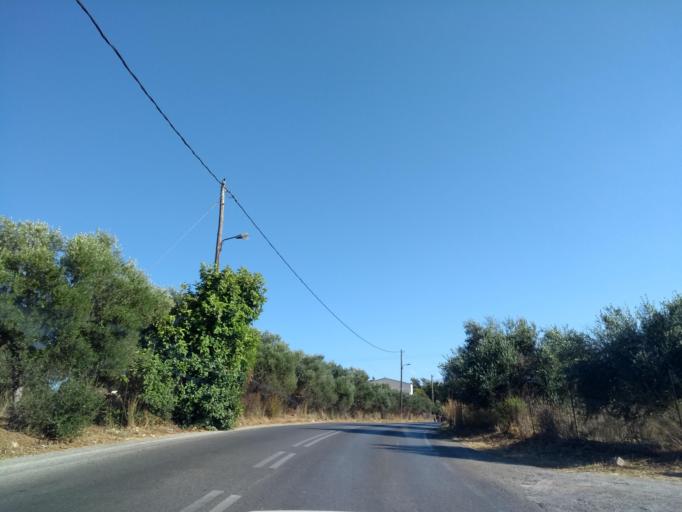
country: GR
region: Crete
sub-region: Nomos Chanias
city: Pithari
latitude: 35.5457
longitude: 24.0825
